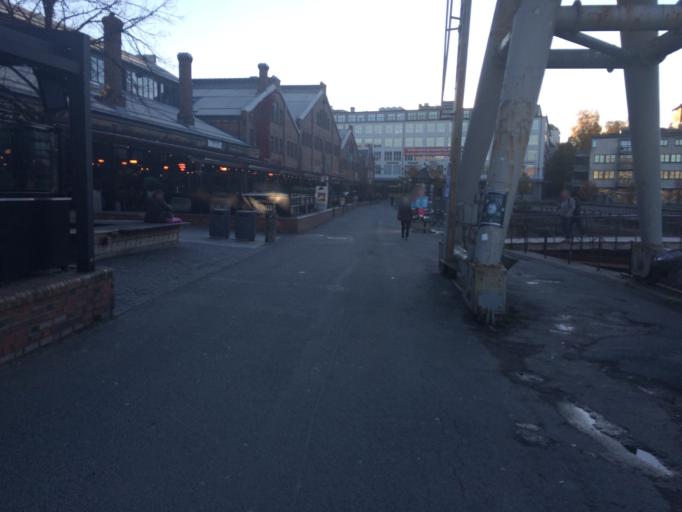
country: NO
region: Sor-Trondelag
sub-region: Trondheim
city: Trondheim
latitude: 63.4347
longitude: 10.4109
